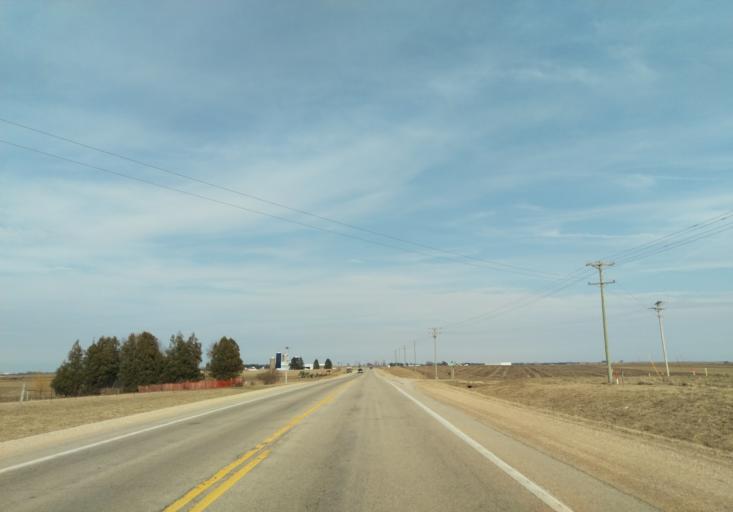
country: US
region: Wisconsin
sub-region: Grant County
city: Lancaster
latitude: 42.9650
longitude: -90.9043
